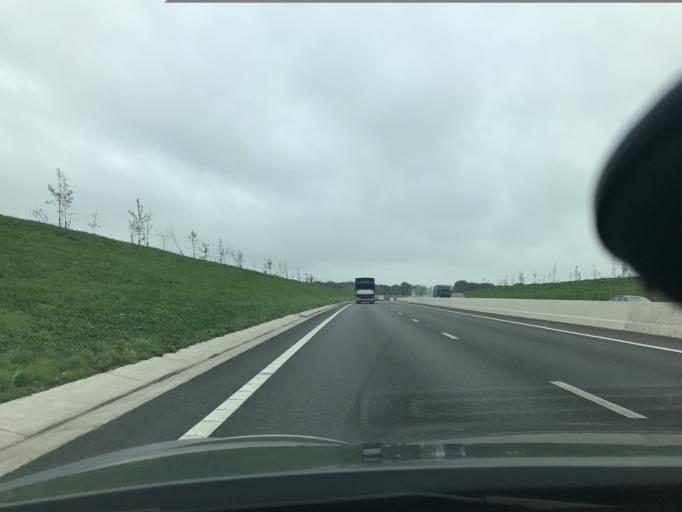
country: GB
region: England
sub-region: Cheshire East
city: Mere
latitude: 53.3422
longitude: -2.4146
